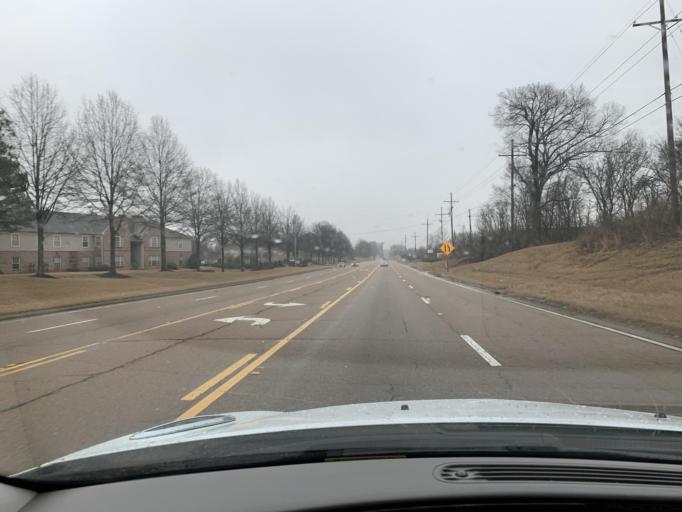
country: US
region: Mississippi
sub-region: De Soto County
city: Horn Lake
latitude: 34.9310
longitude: -90.0124
